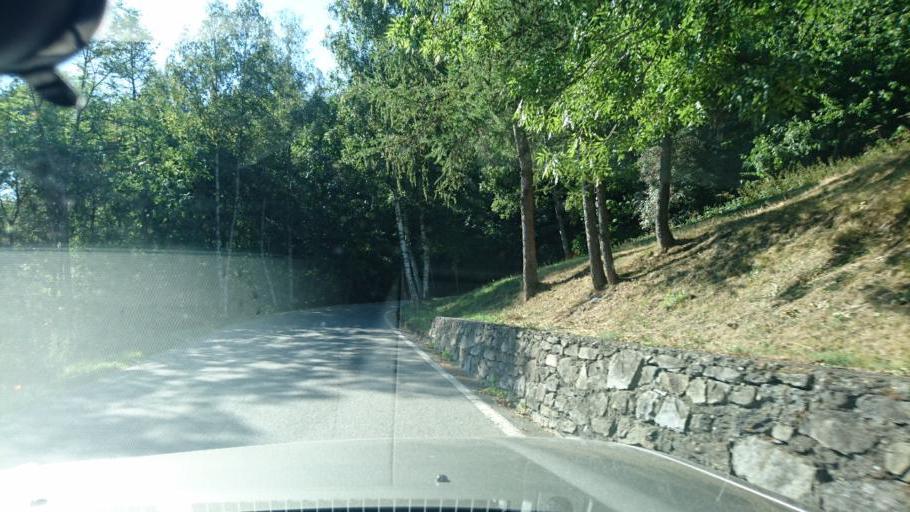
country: IT
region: Aosta Valley
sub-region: Valle d'Aosta
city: Morgex
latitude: 45.7487
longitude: 7.0399
